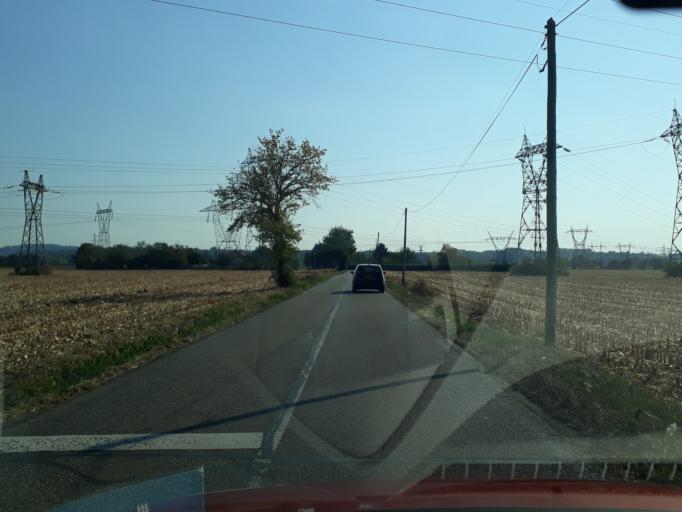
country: FR
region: Rhone-Alpes
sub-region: Departement du Rhone
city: Toussieu
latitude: 45.6823
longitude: 4.9831
